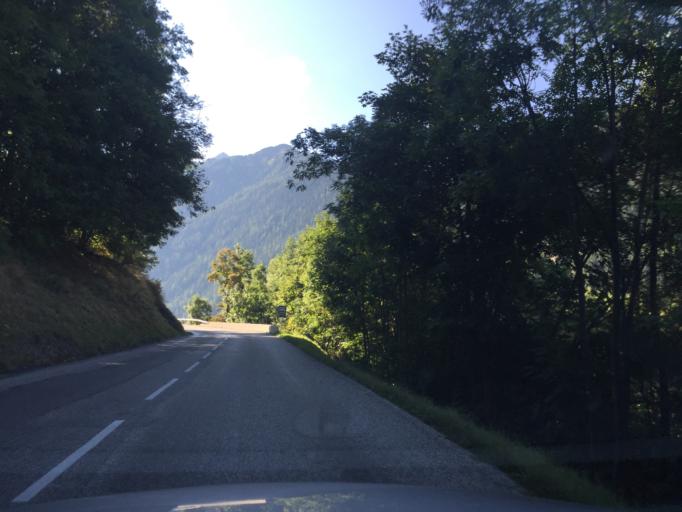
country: FR
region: Rhone-Alpes
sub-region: Departement de la Savoie
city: Belle-Plagne
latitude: 45.5471
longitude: 6.7534
